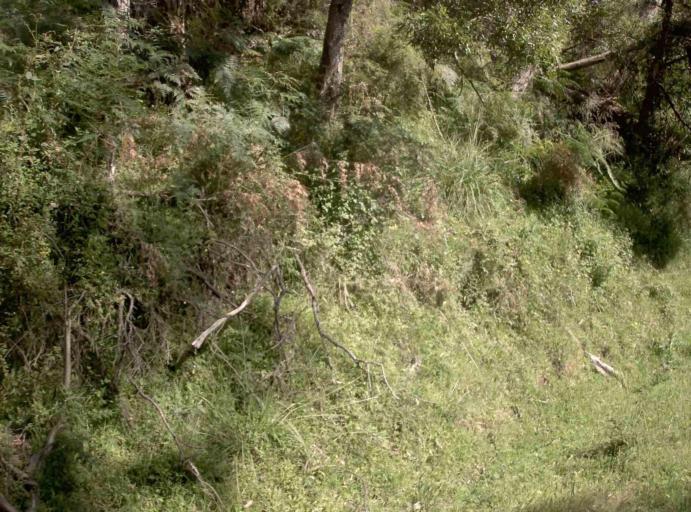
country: AU
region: New South Wales
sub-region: Bombala
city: Bombala
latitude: -37.3454
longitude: 148.6934
